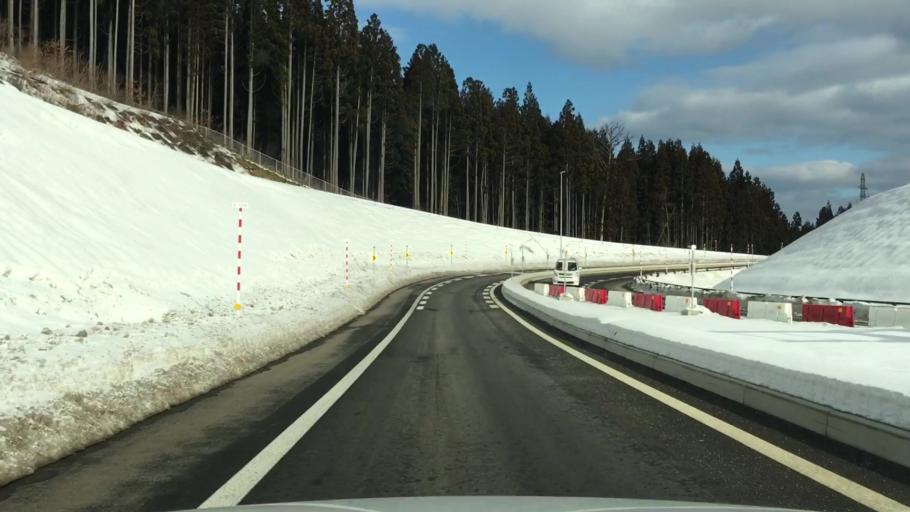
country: JP
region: Akita
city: Takanosu
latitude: 40.1992
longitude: 140.3731
